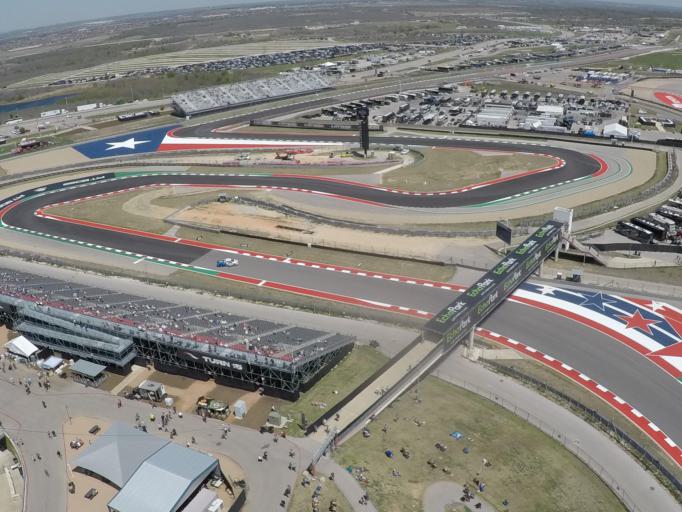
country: US
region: Texas
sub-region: Travis County
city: Garfield
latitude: 30.1341
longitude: -97.6378
